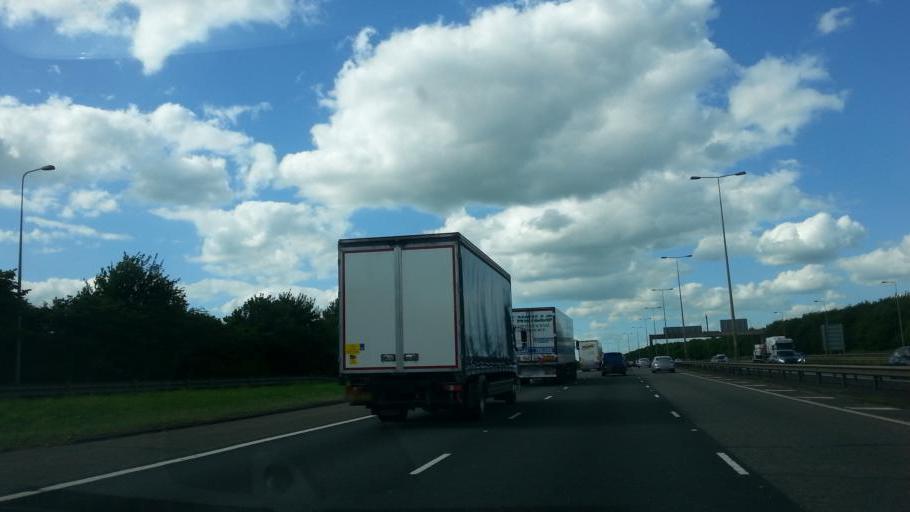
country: GB
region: England
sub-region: Cambridgeshire
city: Stilton
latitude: 52.5051
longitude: -0.2943
